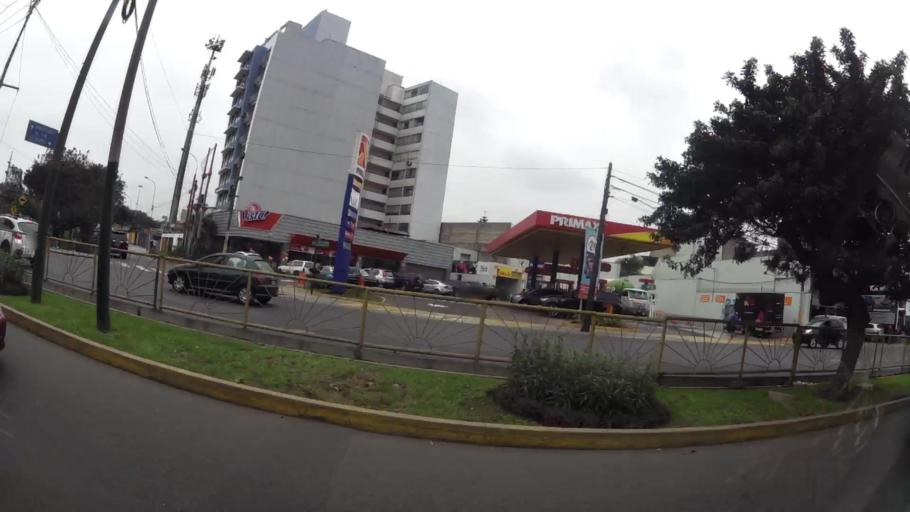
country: PE
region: Lima
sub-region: Lima
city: San Luis
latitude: -12.1109
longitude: -76.9773
